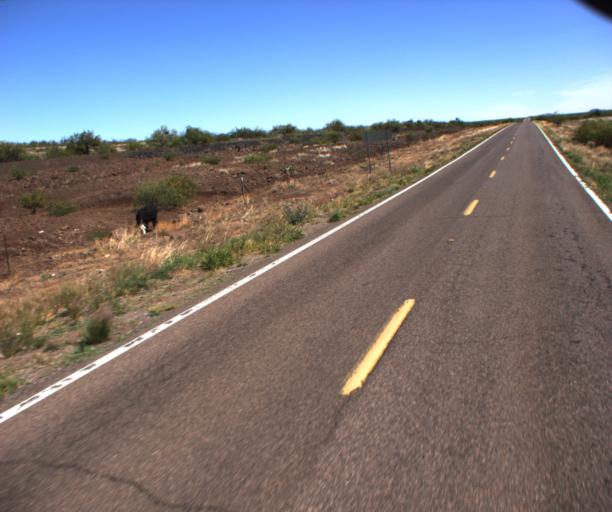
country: US
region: Arizona
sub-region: Cochise County
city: Douglas
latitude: 31.4708
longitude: -109.3584
